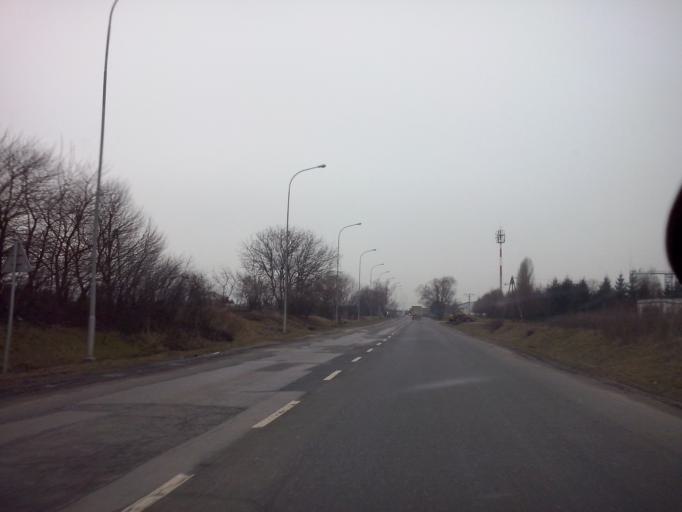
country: PL
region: Lublin Voivodeship
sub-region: Zamosc
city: Zamosc
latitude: 50.7362
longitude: 23.2427
